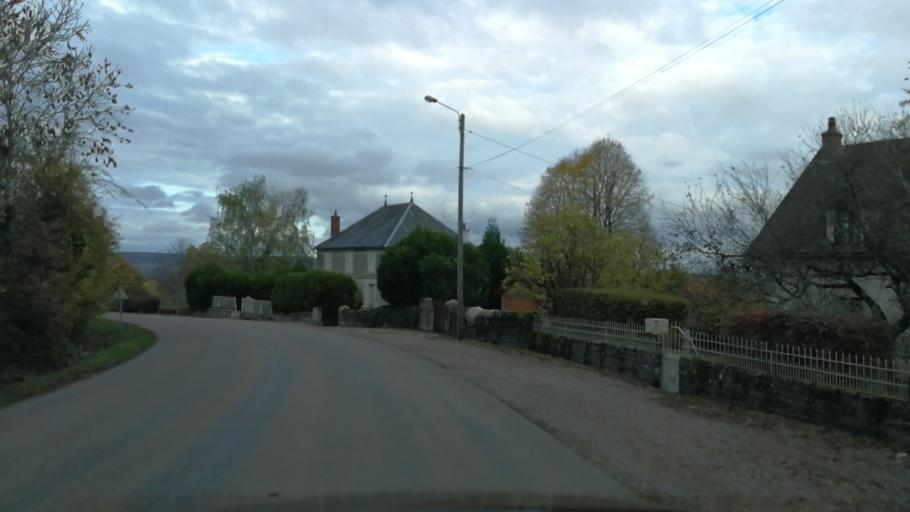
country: FR
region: Bourgogne
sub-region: Departement de la Cote-d'Or
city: Saulieu
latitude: 47.2628
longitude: 4.3467
